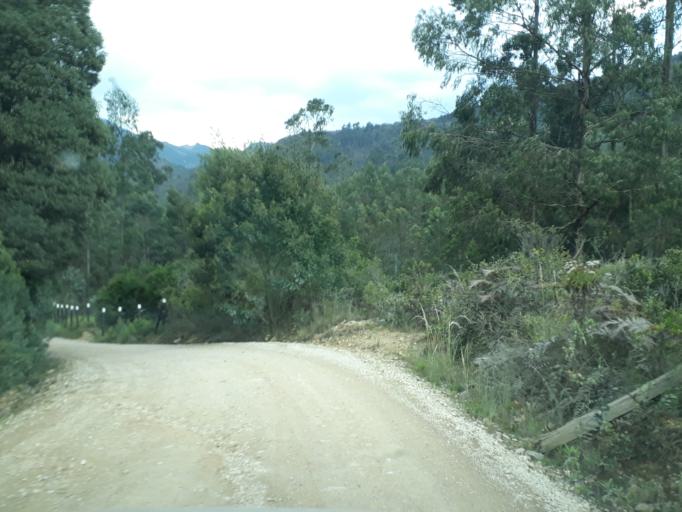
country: CO
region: Cundinamarca
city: Lenguazaque
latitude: 5.2647
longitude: -73.6932
